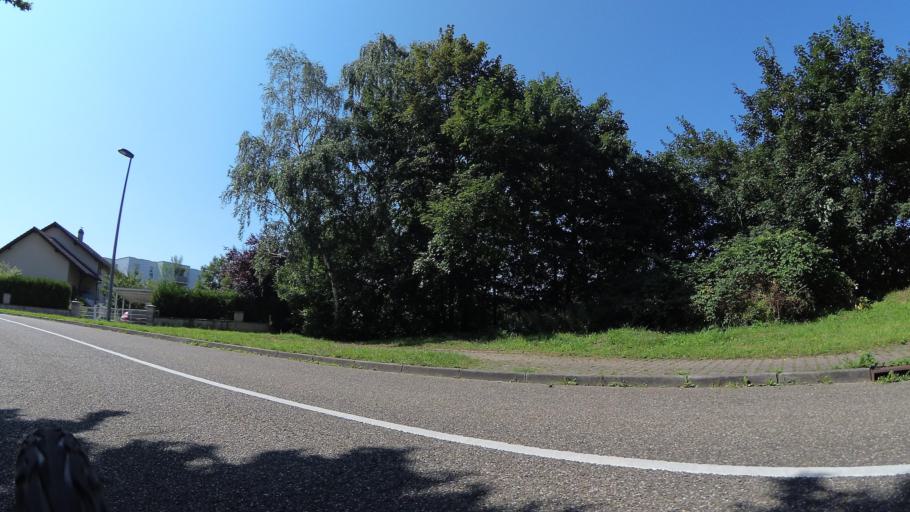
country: FR
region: Lorraine
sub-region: Departement de la Moselle
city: Stiring-Wendel
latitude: 49.2073
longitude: 6.9400
